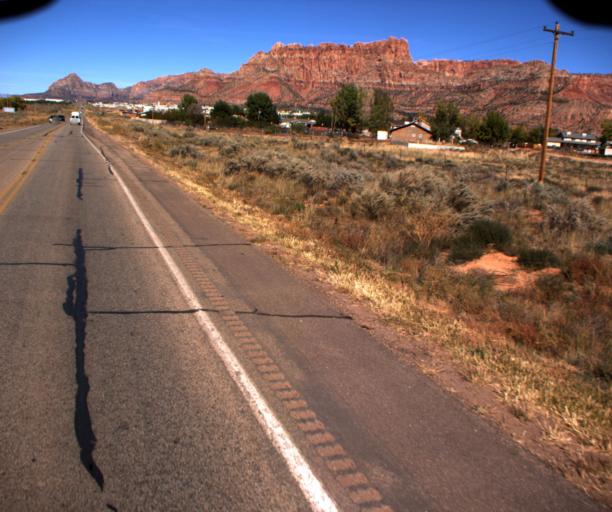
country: US
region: Arizona
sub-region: Mohave County
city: Colorado City
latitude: 36.9837
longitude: -112.9856
